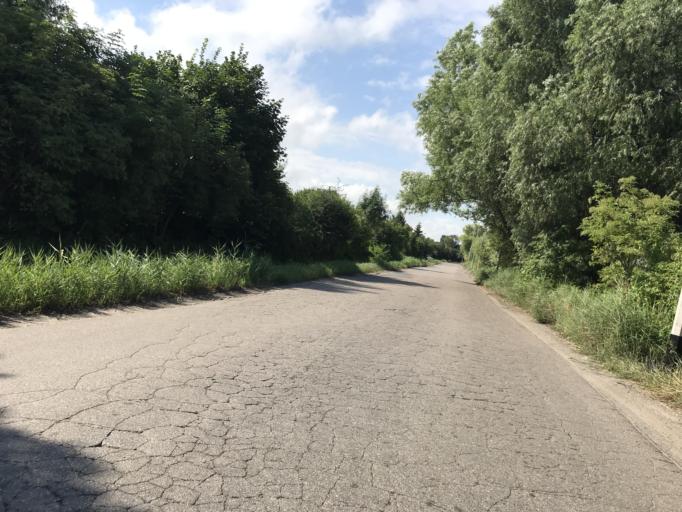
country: PL
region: Pomeranian Voivodeship
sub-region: Gdansk
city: Gdansk
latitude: 54.3382
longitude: 18.6617
